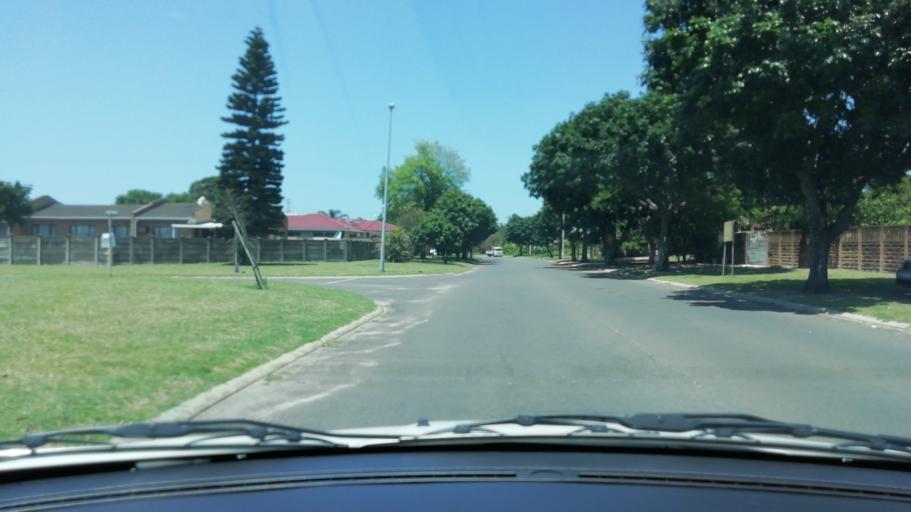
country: ZA
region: KwaZulu-Natal
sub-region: uThungulu District Municipality
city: Richards Bay
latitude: -28.7340
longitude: 32.0457
